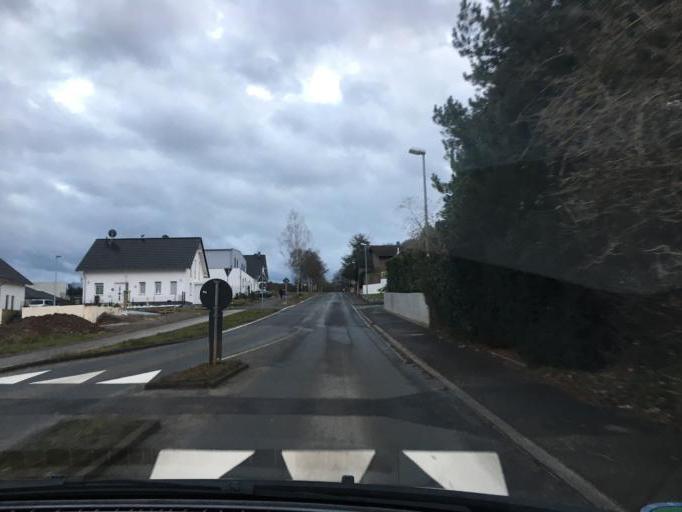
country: DE
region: North Rhine-Westphalia
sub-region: Regierungsbezirk Koln
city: Mechernich
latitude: 50.6072
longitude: 6.6510
